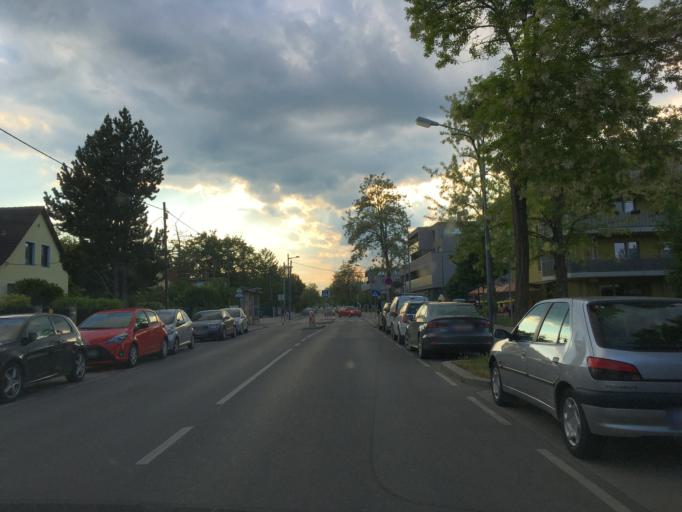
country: AT
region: Lower Austria
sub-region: Politischer Bezirk Wien-Umgebung
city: Gerasdorf bei Wien
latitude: 48.2859
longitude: 16.4357
